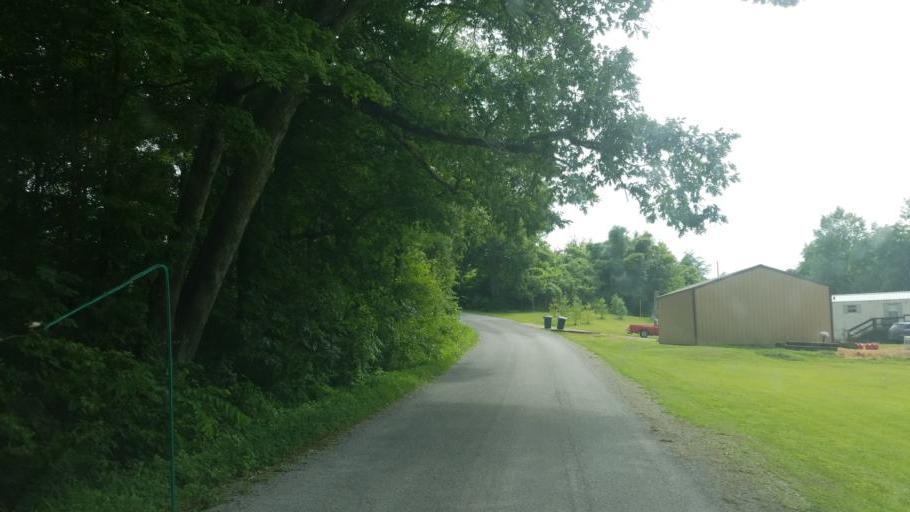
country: US
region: Illinois
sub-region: Union County
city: Cobden
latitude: 37.6187
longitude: -89.3705
